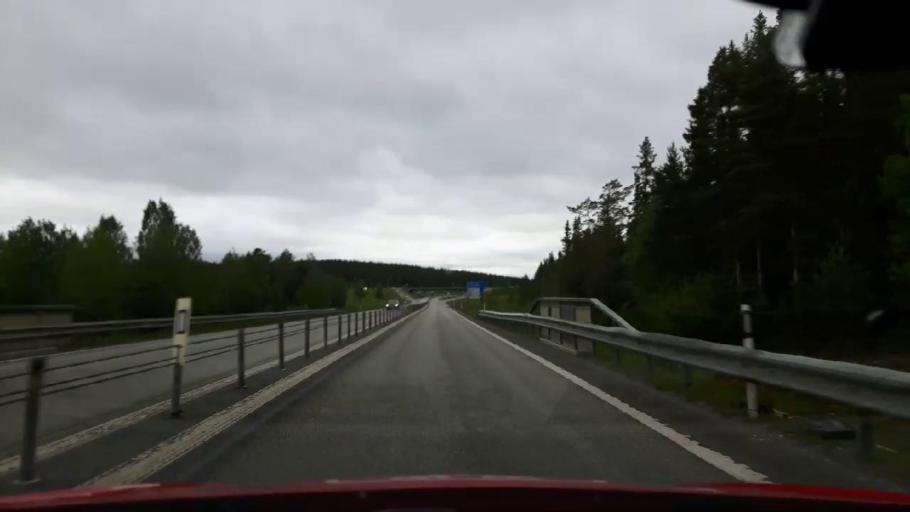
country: SE
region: Jaemtland
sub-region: OEstersunds Kommun
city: Ostersund
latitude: 63.1772
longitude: 14.6944
